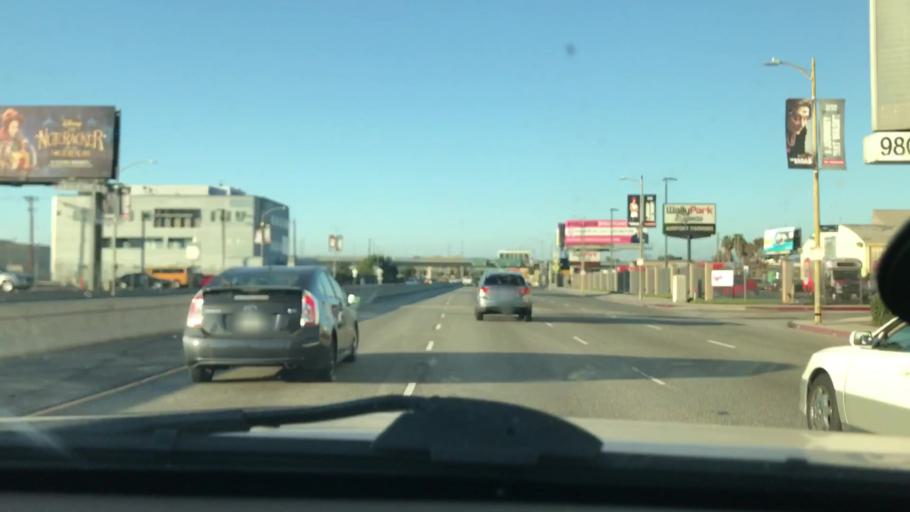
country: US
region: California
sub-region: Los Angeles County
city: El Segundo
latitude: 33.9470
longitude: -118.3961
